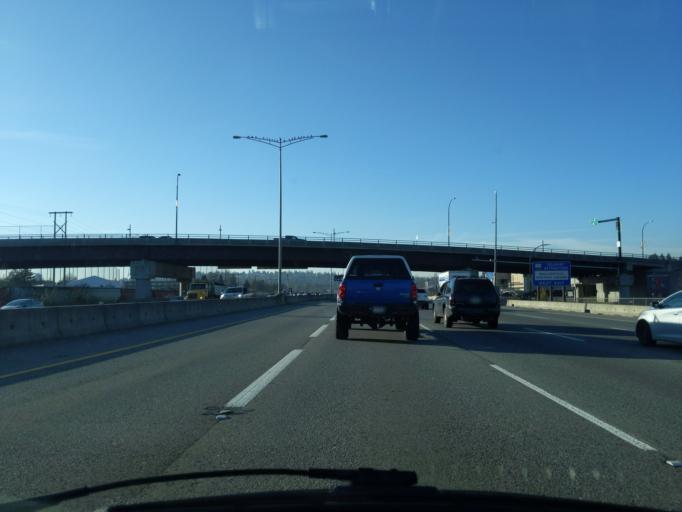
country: CA
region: British Columbia
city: Port Moody
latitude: 49.2315
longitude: -122.8608
